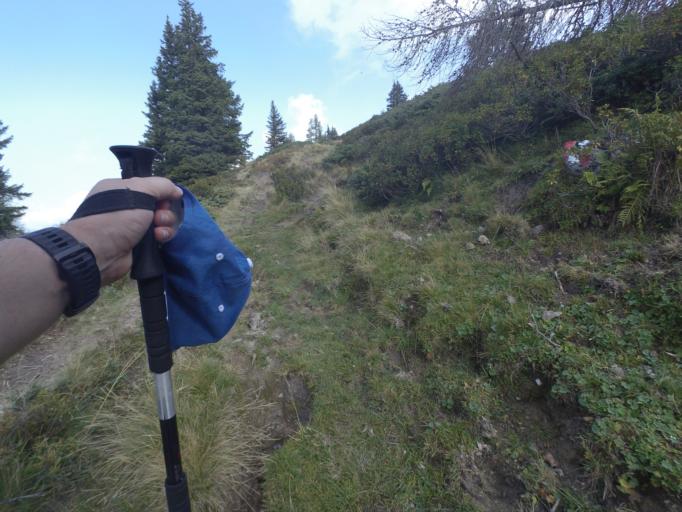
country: AT
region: Salzburg
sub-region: Politischer Bezirk Sankt Johann im Pongau
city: Kleinarl
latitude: 47.2628
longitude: 13.2767
